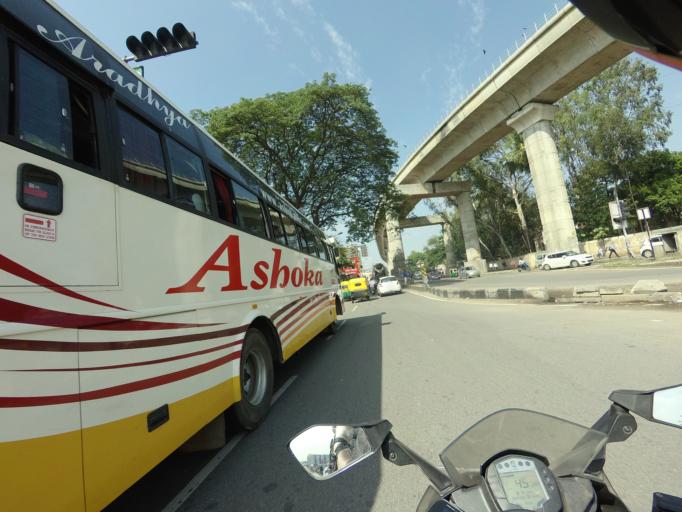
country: IN
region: Karnataka
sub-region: Bangalore Urban
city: Bangalore
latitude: 12.9504
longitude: 77.5375
